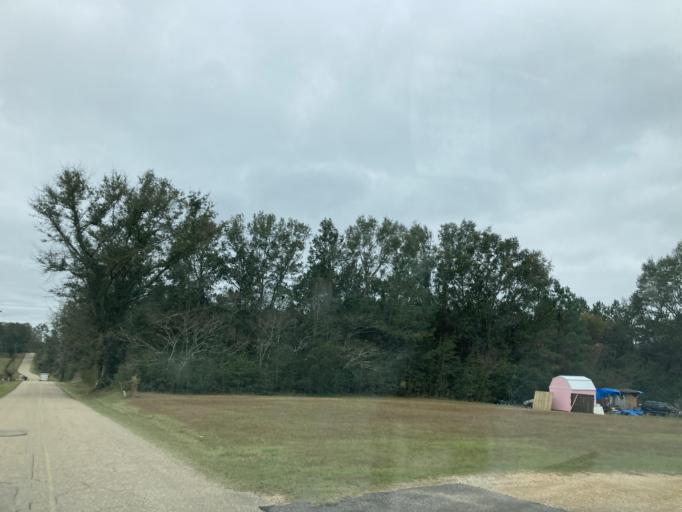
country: US
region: Mississippi
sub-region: Lamar County
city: West Hattiesburg
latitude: 31.2684
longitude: -89.5059
